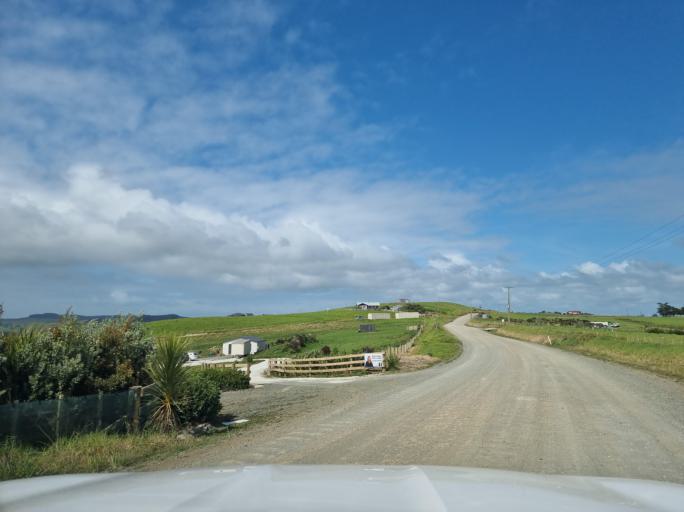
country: NZ
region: Auckland
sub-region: Auckland
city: Wellsford
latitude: -36.1387
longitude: 174.4972
